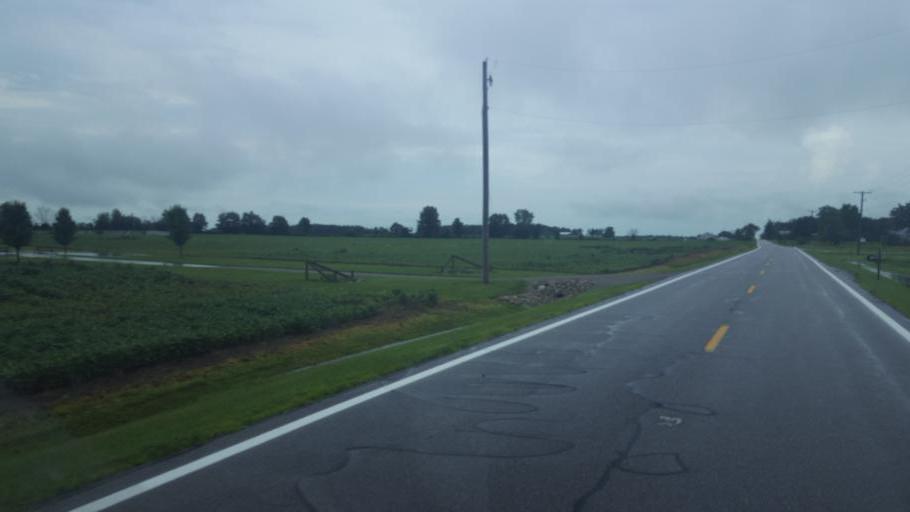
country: US
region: Ohio
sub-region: Union County
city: Richwood
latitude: 40.5003
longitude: -83.2882
